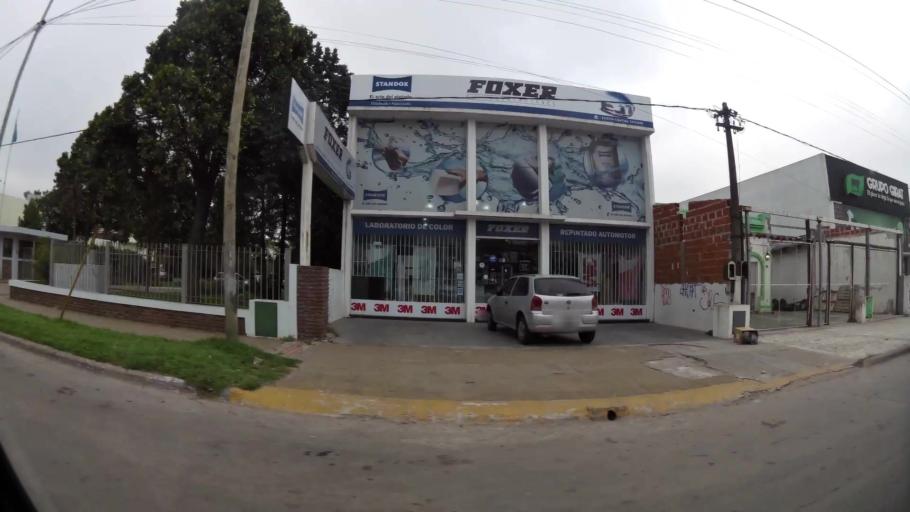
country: AR
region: Buenos Aires
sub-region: Partido de La Plata
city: La Plata
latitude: -34.9424
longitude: -57.9900
